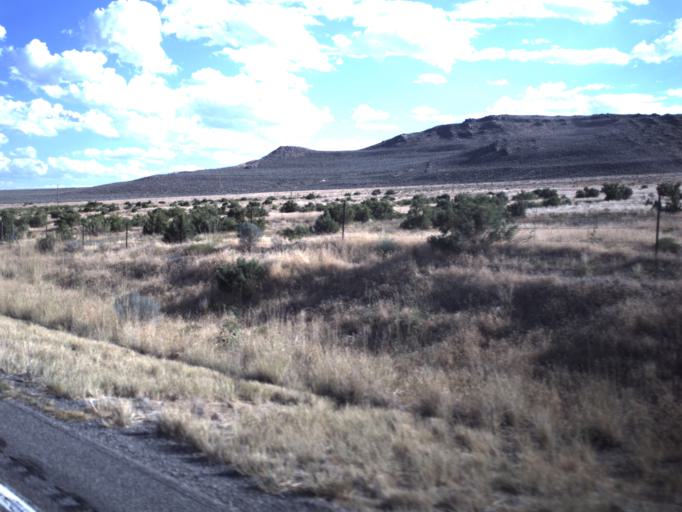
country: US
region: Utah
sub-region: Tooele County
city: Grantsville
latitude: 40.6464
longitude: -112.5286
